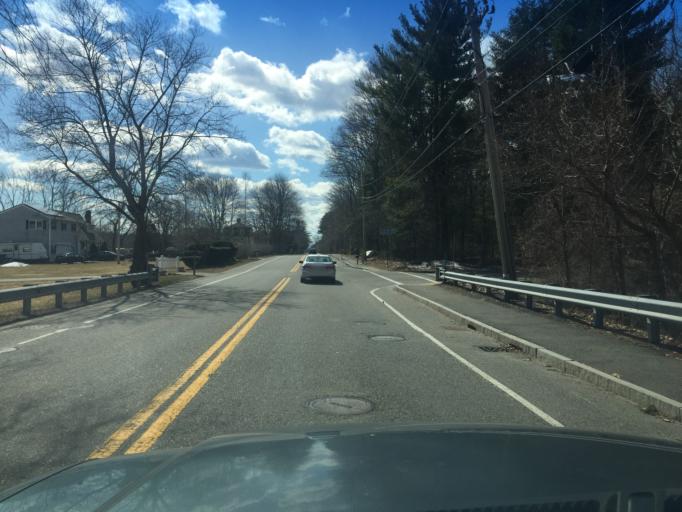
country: US
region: Massachusetts
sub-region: Middlesex County
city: Holliston
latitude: 42.1638
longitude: -71.4436
